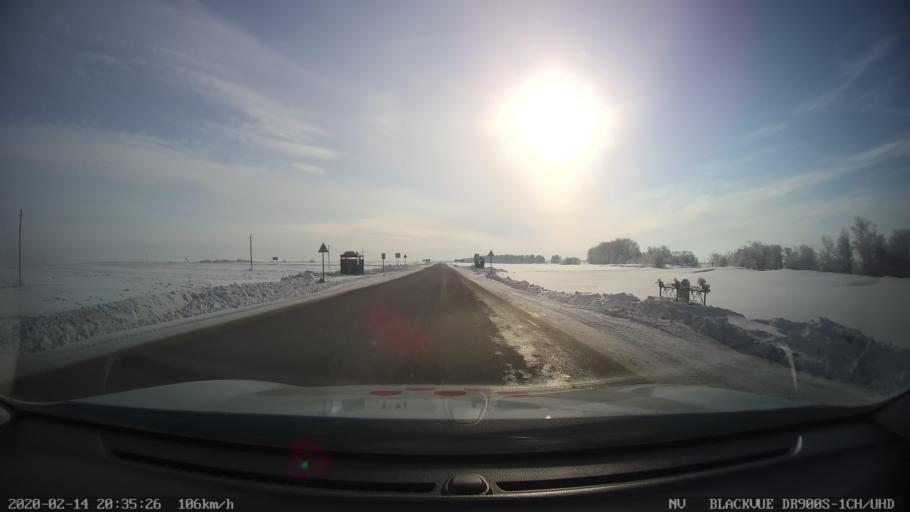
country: RU
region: Tatarstan
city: Kuybyshevskiy Zaton
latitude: 55.3823
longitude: 48.9837
